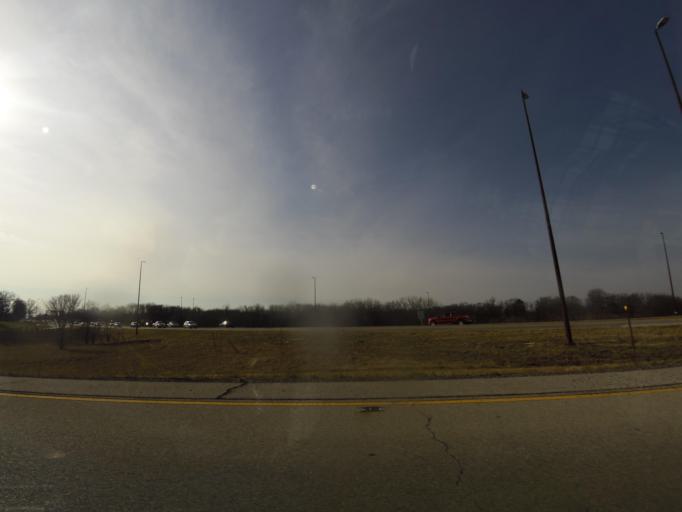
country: US
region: Illinois
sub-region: Macon County
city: Forsyth
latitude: 39.9070
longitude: -88.9548
